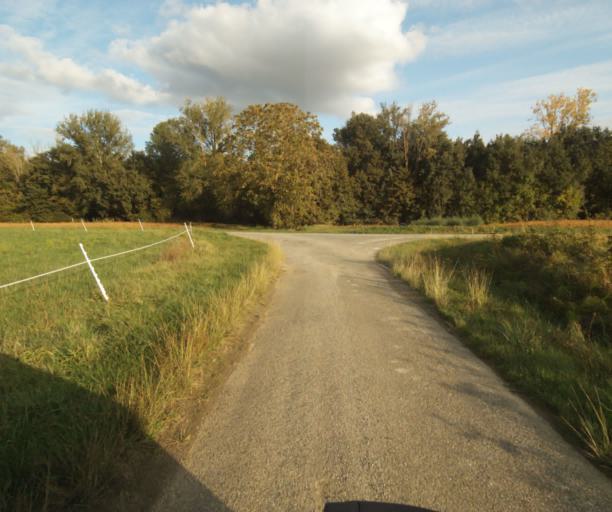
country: FR
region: Midi-Pyrenees
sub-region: Departement de la Haute-Garonne
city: Launac
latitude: 43.8301
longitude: 1.1351
